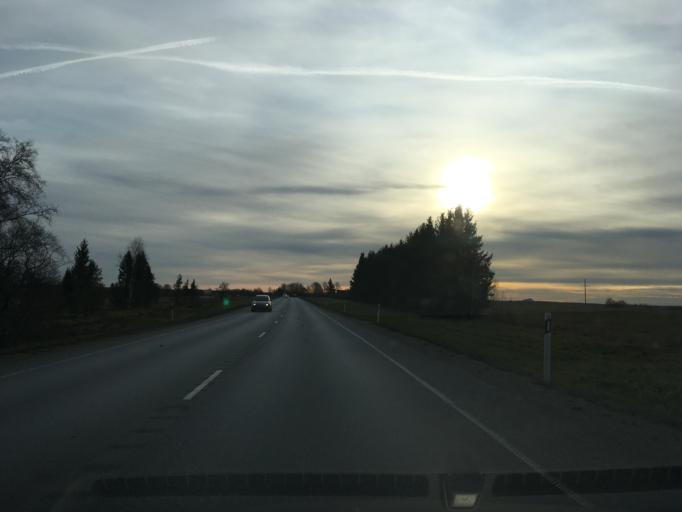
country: EE
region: Ida-Virumaa
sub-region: Kivioli linn
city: Kivioli
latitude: 59.4181
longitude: 26.9738
